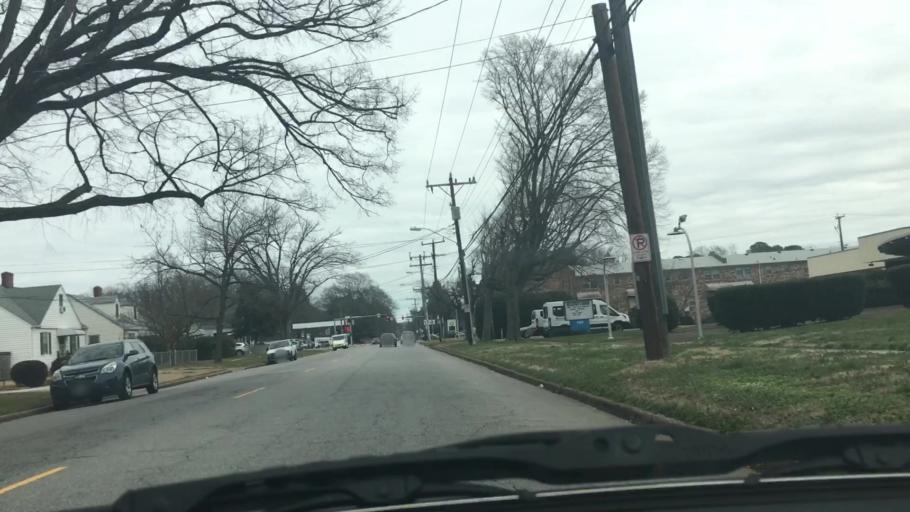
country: US
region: Virginia
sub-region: City of Norfolk
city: Norfolk
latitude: 36.9336
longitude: -76.2467
